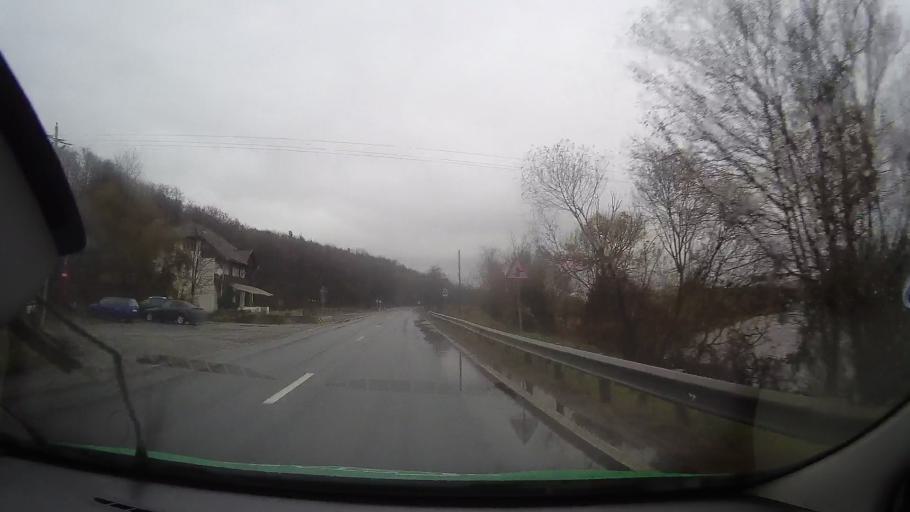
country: RO
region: Mures
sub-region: Comuna Brancovenesti
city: Valenii de Mures
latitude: 46.8776
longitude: 24.7771
